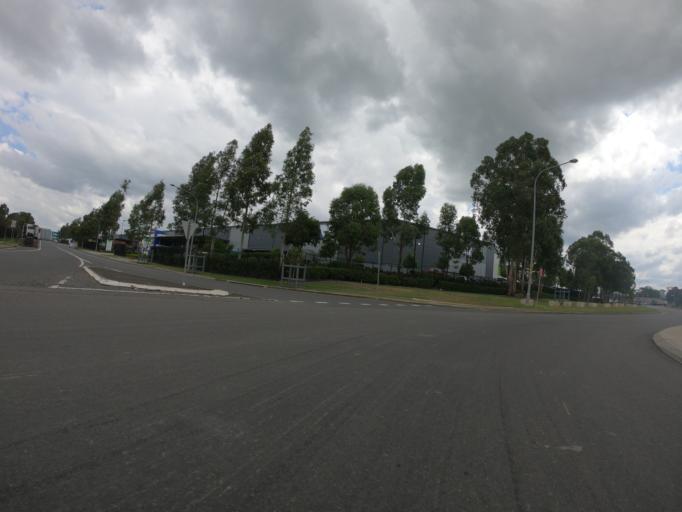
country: AU
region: New South Wales
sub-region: Blacktown
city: Mount Druitt
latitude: -33.8211
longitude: 150.7777
